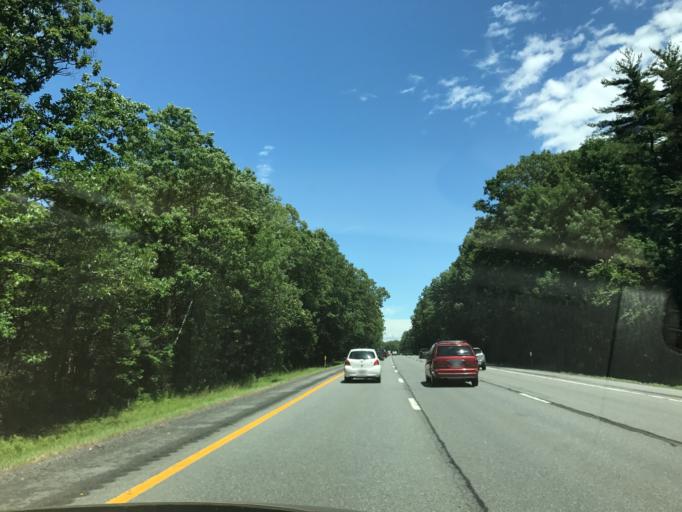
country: US
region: New York
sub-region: Warren County
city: West Glens Falls
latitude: 43.1940
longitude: -73.7019
